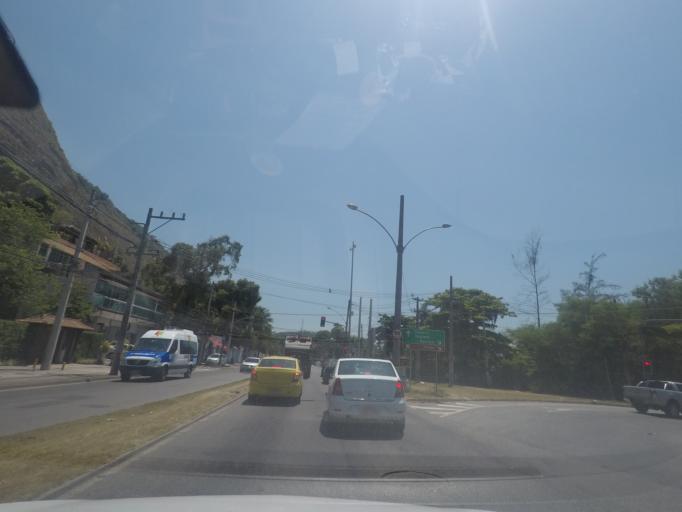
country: BR
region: Rio de Janeiro
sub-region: Nilopolis
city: Nilopolis
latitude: -22.9928
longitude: -43.4474
